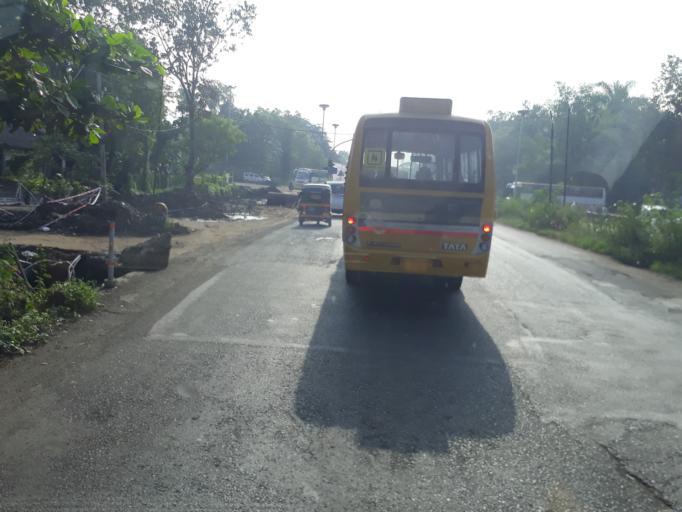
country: IN
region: Maharashtra
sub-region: Raigarh
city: Kalundri
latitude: 18.9749
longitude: 73.1241
